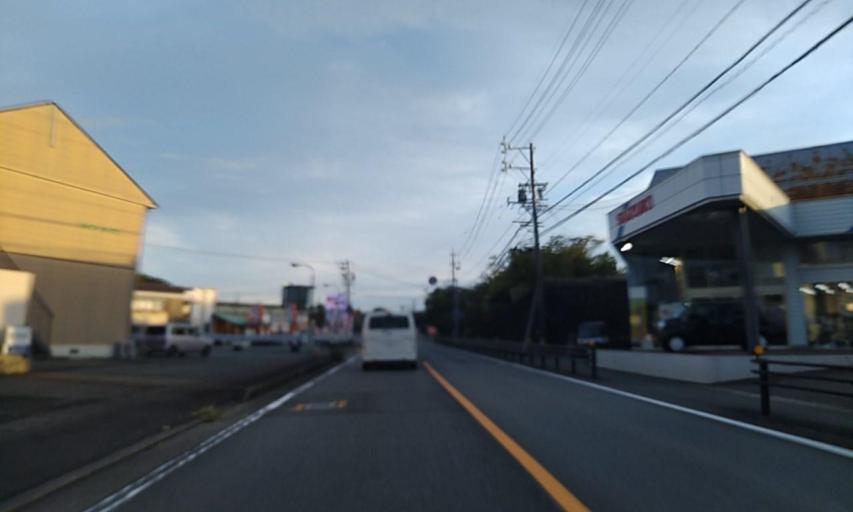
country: JP
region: Mie
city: Toba
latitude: 34.3262
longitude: 136.8409
